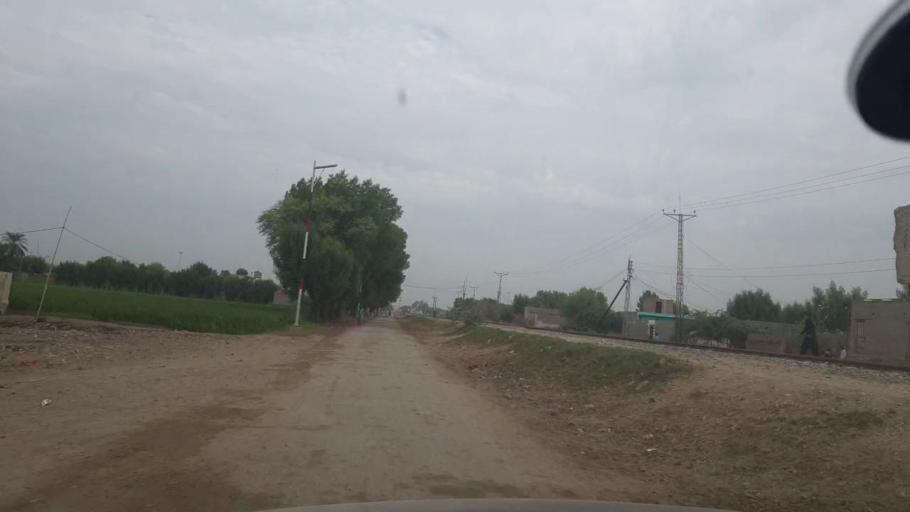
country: PK
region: Sindh
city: Jacobabad
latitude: 28.2648
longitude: 68.4453
